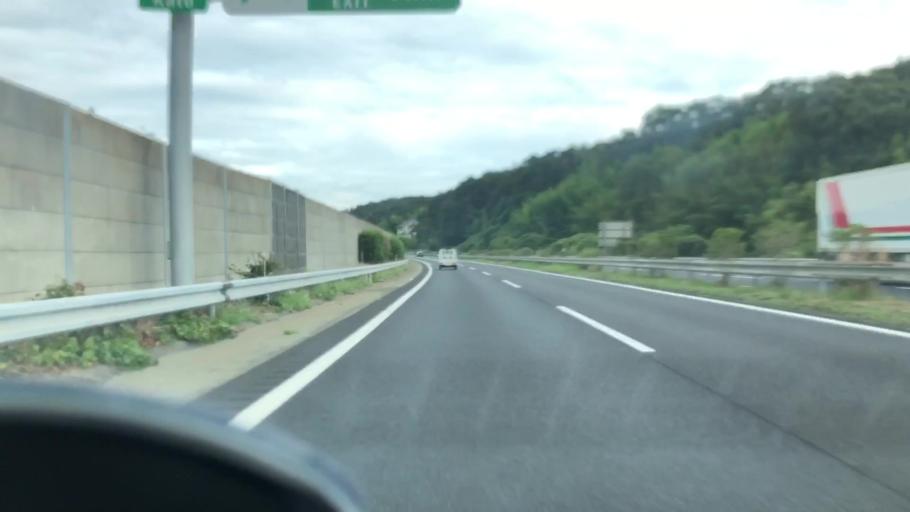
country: JP
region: Hyogo
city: Yashiro
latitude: 34.9014
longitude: 135.0689
